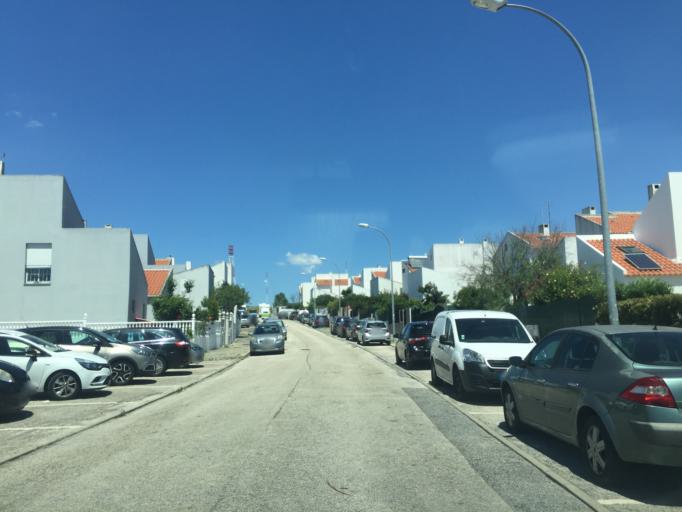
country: PT
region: Lisbon
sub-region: Oeiras
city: Quejas
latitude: 38.7231
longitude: -9.2672
